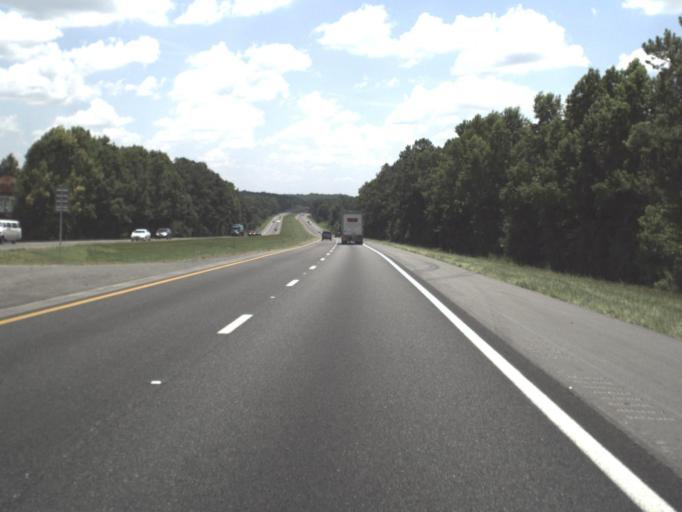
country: US
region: Florida
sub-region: Madison County
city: Madison
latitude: 30.4351
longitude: -83.4882
